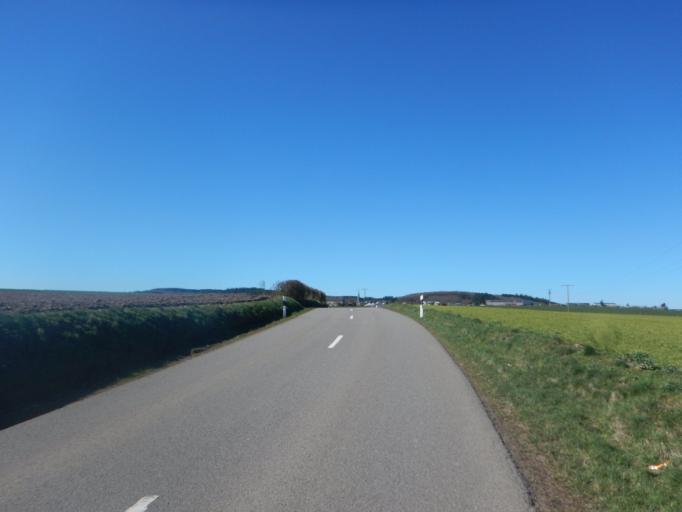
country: LU
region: Diekirch
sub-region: Canton de Wiltz
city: Eschweiler
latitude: 49.9918
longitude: 5.9546
